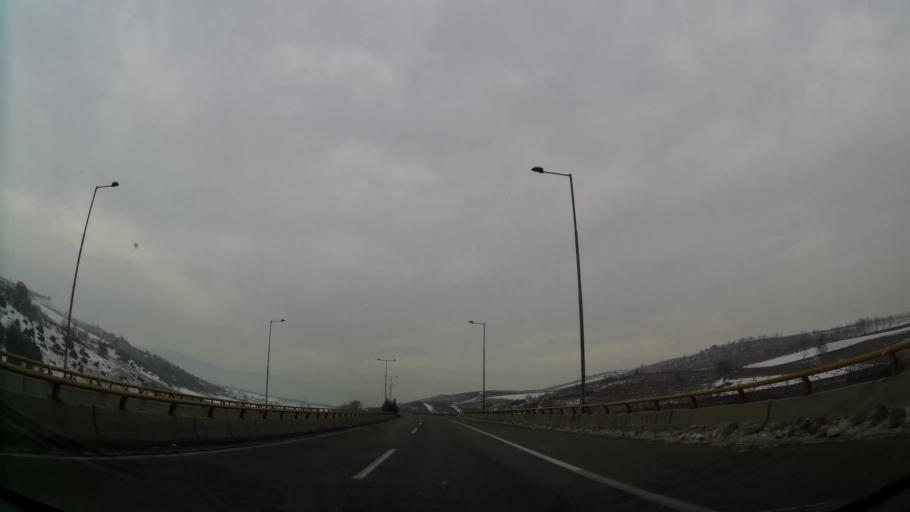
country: MK
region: Saraj
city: Saraj
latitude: 42.0175
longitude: 21.3315
